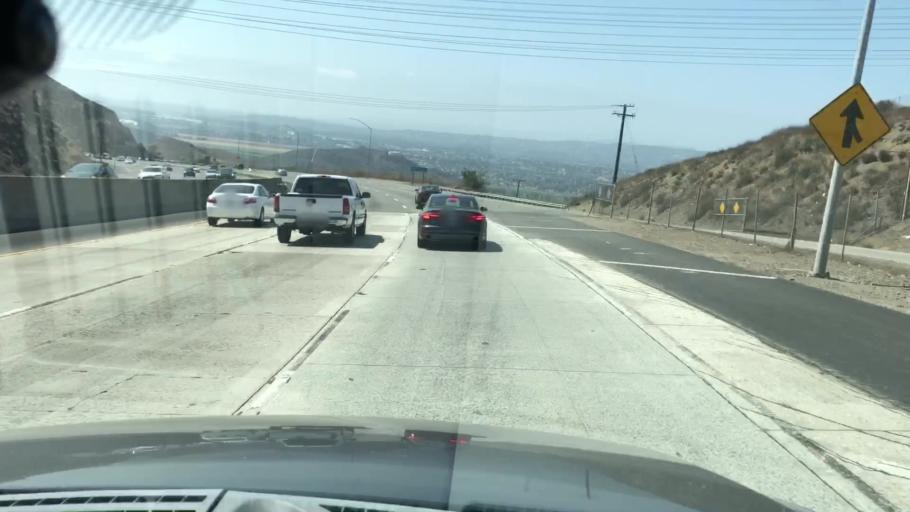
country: US
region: California
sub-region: Ventura County
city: Casa Conejo
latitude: 34.2001
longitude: -118.9572
